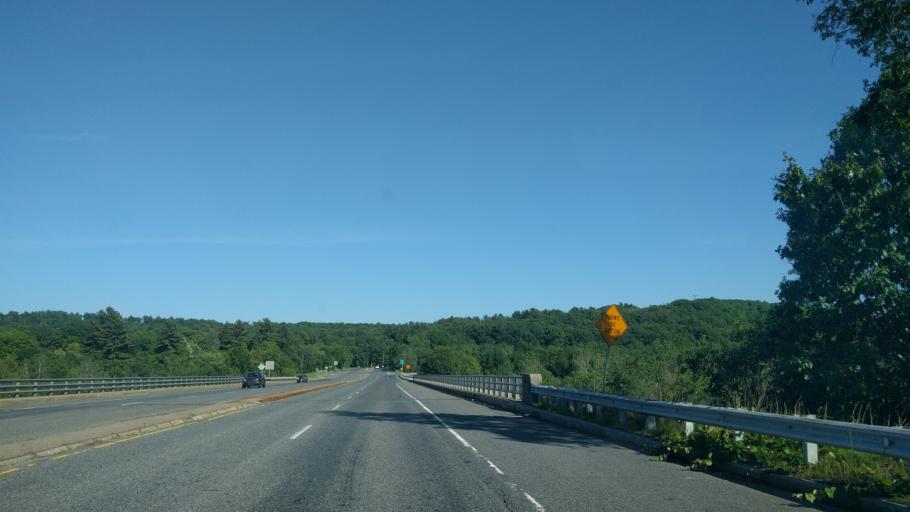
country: US
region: Massachusetts
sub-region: Worcester County
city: Oxford
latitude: 42.1513
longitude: -71.8578
